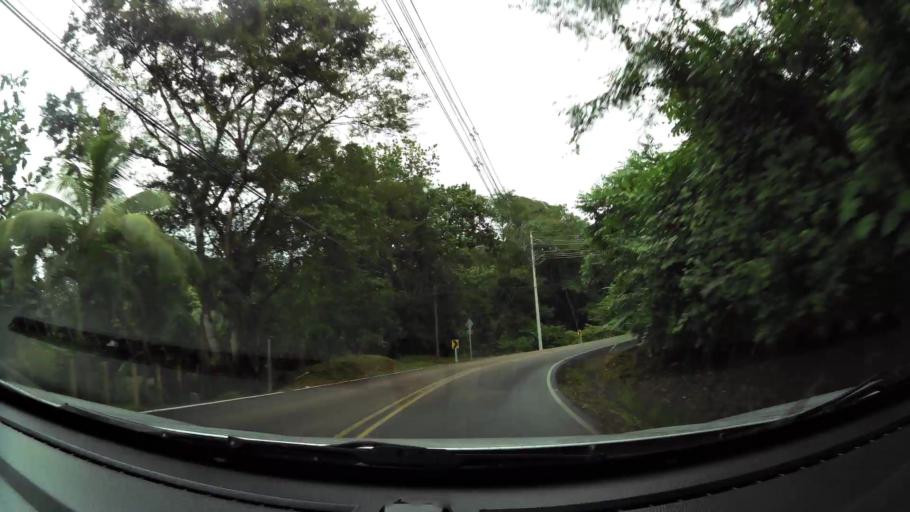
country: CR
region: Puntarenas
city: Esparza
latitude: 9.9609
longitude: -84.6060
